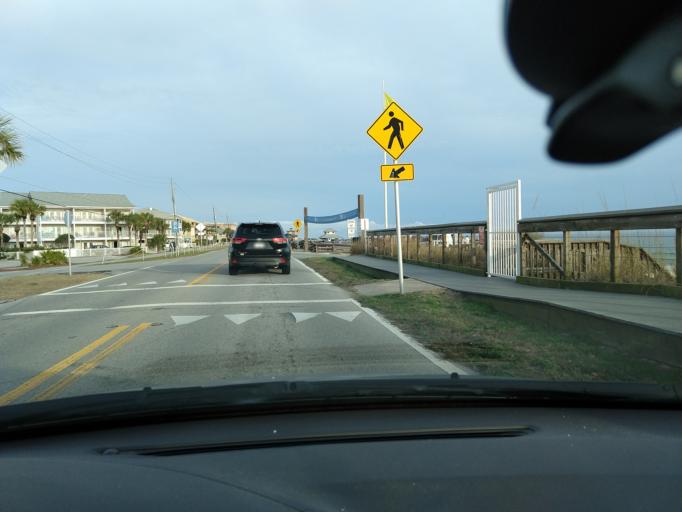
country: US
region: Florida
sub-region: Walton County
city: Miramar Beach
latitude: 30.3786
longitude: -86.3893
